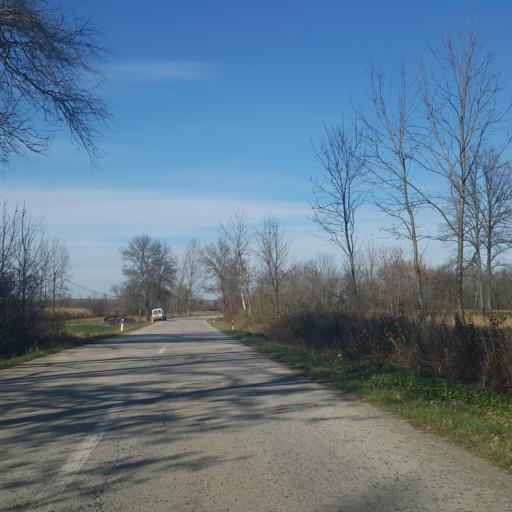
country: RS
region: Central Serbia
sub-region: Sumadijski Okrug
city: Topola
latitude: 44.2493
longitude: 20.8302
